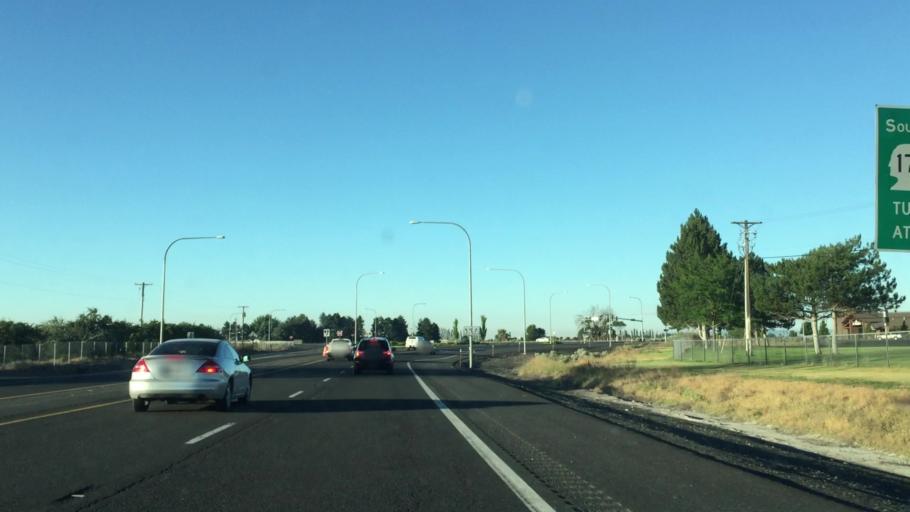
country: US
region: Washington
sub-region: Grant County
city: Moses Lake
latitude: 47.1134
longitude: -119.2537
